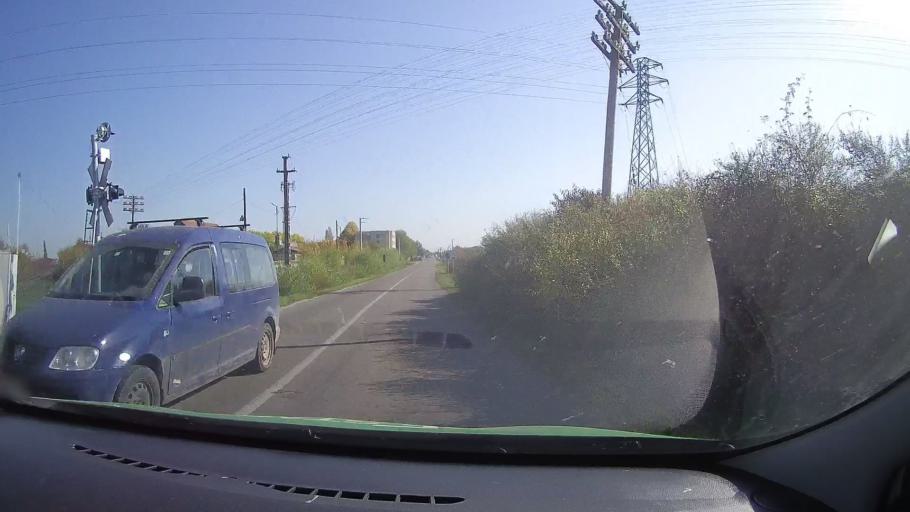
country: RO
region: Satu Mare
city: Carei
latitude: 47.6929
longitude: 22.4413
